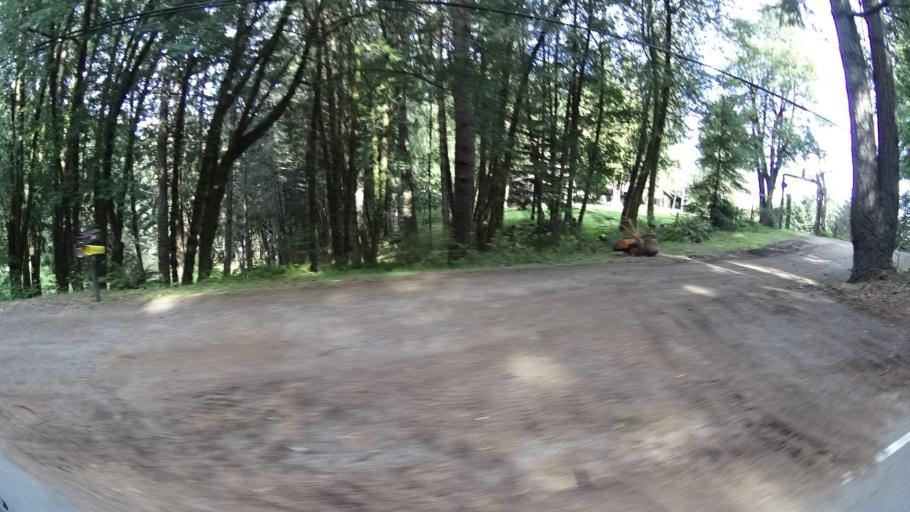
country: US
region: California
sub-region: Humboldt County
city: Blue Lake
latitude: 40.7399
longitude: -123.9533
